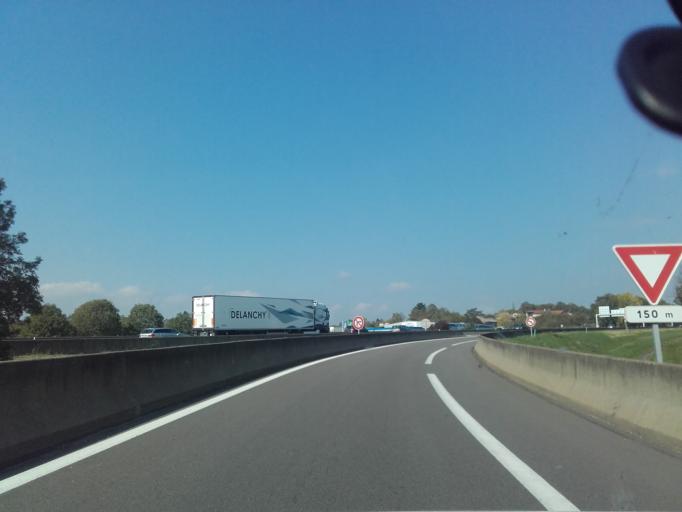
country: FR
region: Bourgogne
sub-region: Departement de Saone-et-Loire
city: Charnay-les-Macon
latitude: 46.2855
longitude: 4.7903
